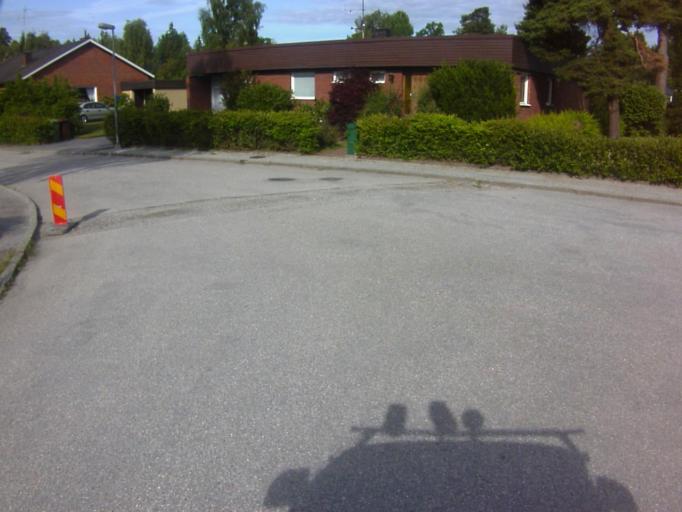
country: SE
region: Soedermanland
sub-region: Eskilstuna Kommun
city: Eskilstuna
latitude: 59.3543
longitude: 16.5169
